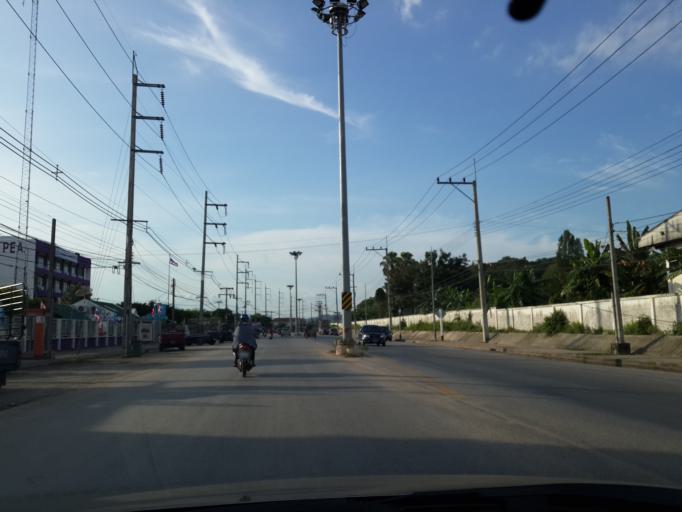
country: TH
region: Yala
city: Yala
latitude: 6.5145
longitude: 101.2720
